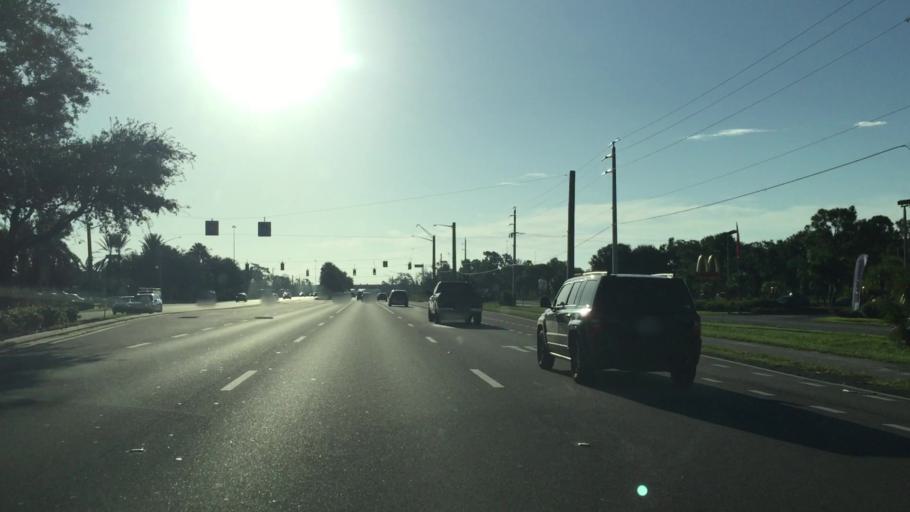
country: US
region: Florida
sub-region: Lee County
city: Gateway
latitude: 26.5472
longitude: -81.8014
